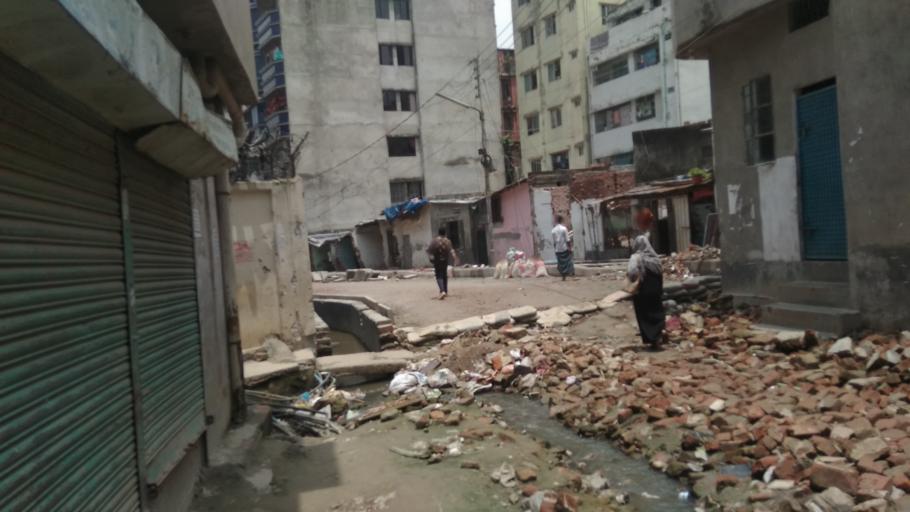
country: BD
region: Dhaka
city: Tungi
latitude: 23.8149
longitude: 90.3706
